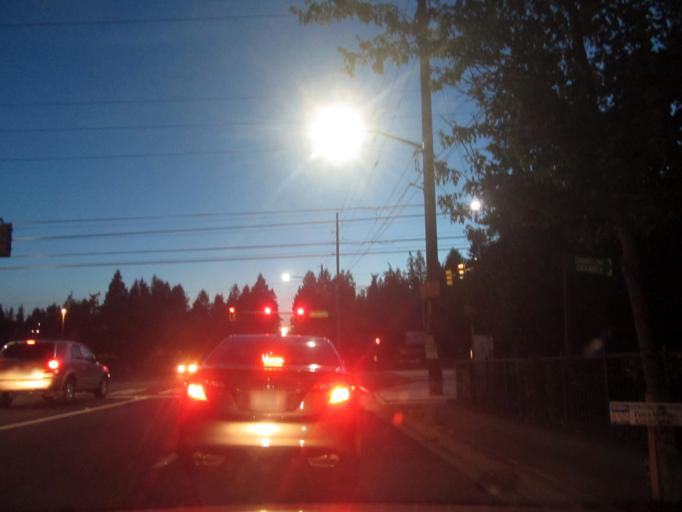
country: US
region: Washington
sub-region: King County
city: Shoreline
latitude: 47.7561
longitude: -122.3344
